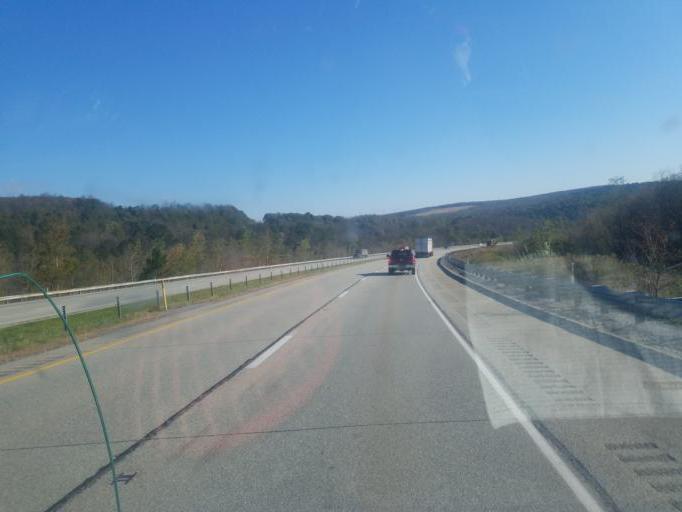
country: US
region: Pennsylvania
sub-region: Cambria County
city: Gallitzin
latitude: 40.4767
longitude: -78.5280
